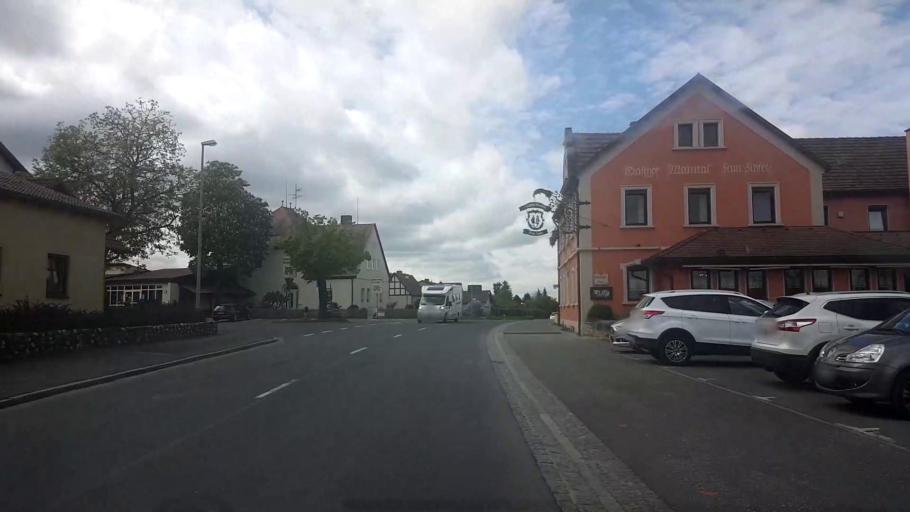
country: DE
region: Bavaria
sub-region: Upper Franconia
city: Lichtenfels
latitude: 50.1234
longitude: 11.0349
